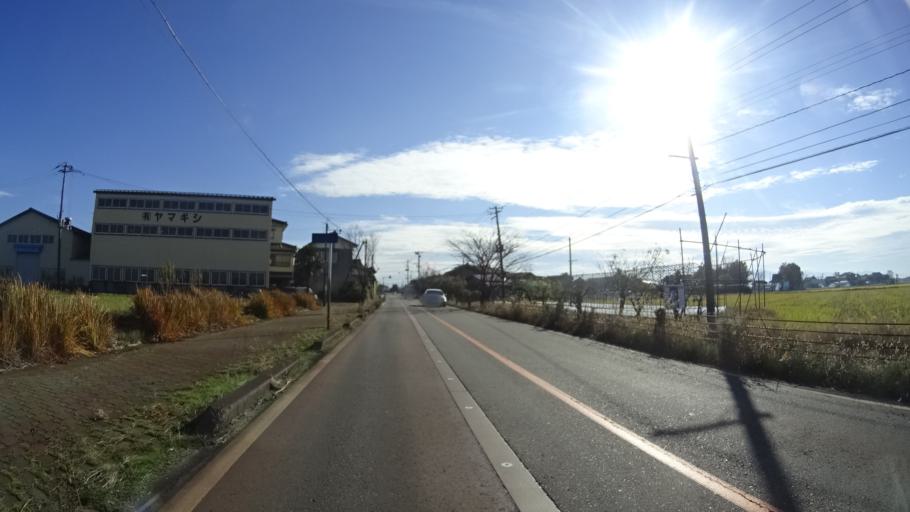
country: JP
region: Niigata
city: Mitsuke
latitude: 37.5522
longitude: 138.8648
